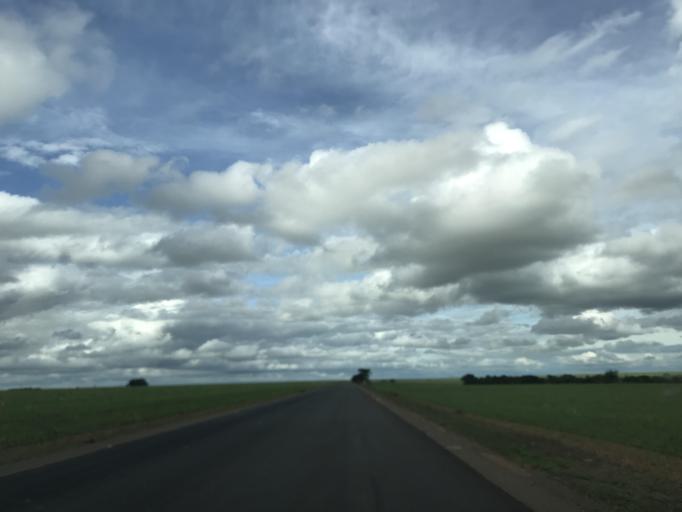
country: BR
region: Goias
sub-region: Vianopolis
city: Vianopolis
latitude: -16.9669
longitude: -48.6489
